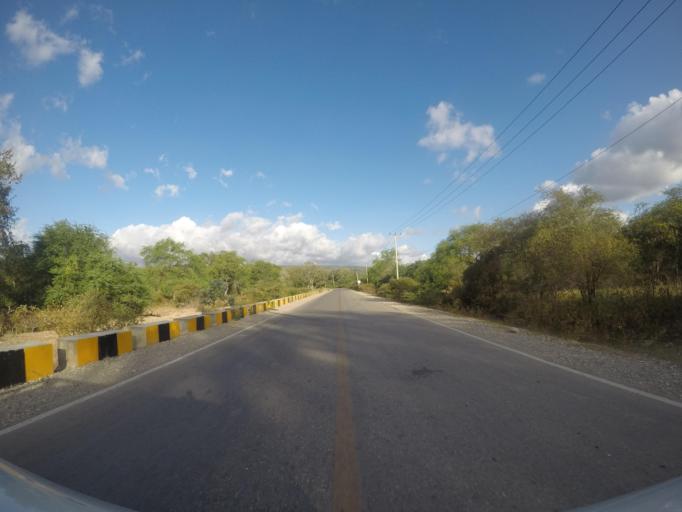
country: TL
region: Lautem
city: Lospalos
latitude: -8.3739
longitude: 126.8867
